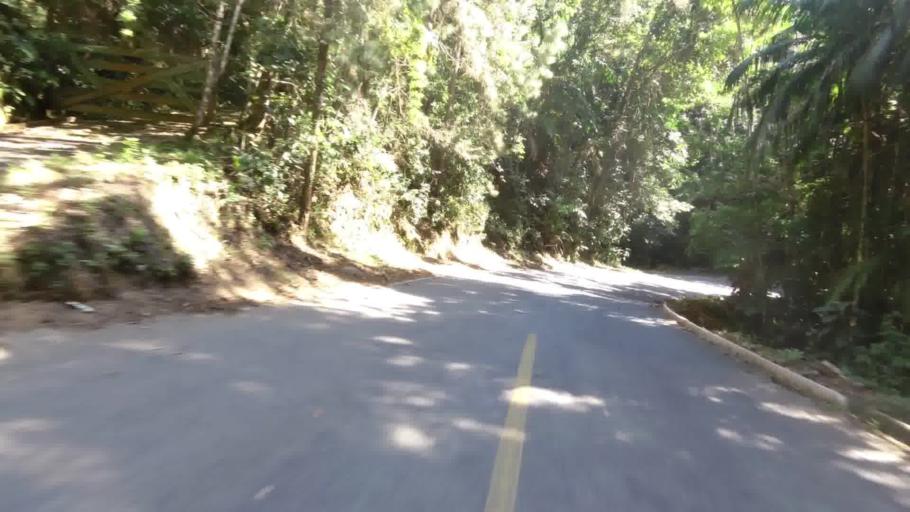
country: BR
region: Espirito Santo
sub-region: Marechal Floriano
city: Marechal Floriano
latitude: -20.4531
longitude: -40.9041
